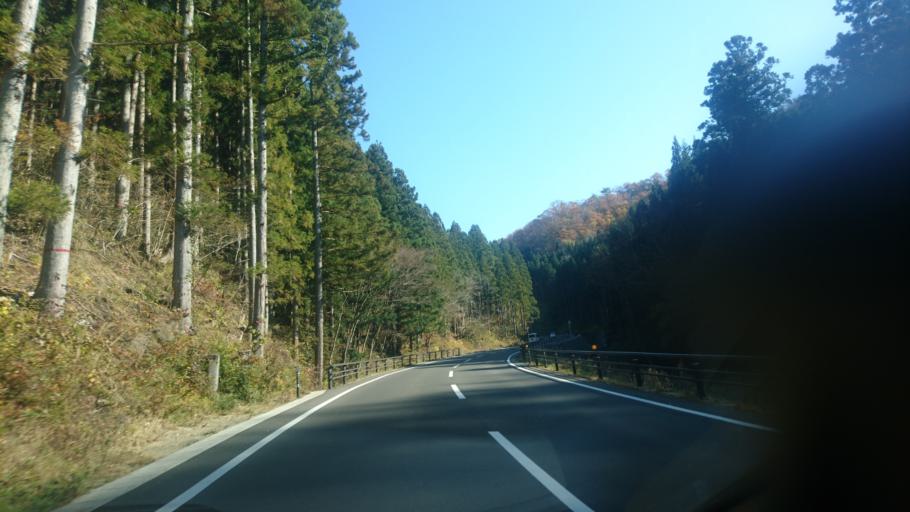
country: JP
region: Miyagi
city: Okawara
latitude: 38.1314
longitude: 140.7672
